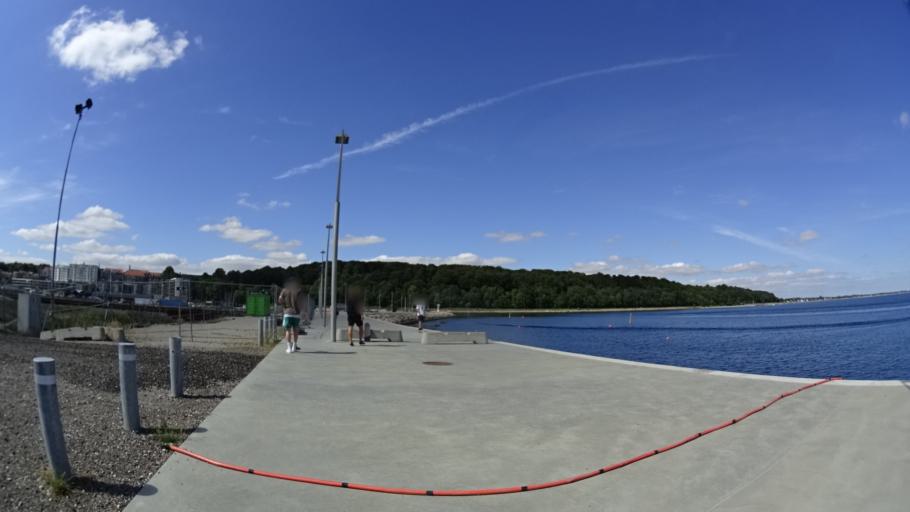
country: DK
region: Central Jutland
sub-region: Arhus Kommune
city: Arhus
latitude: 56.1677
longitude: 10.2280
